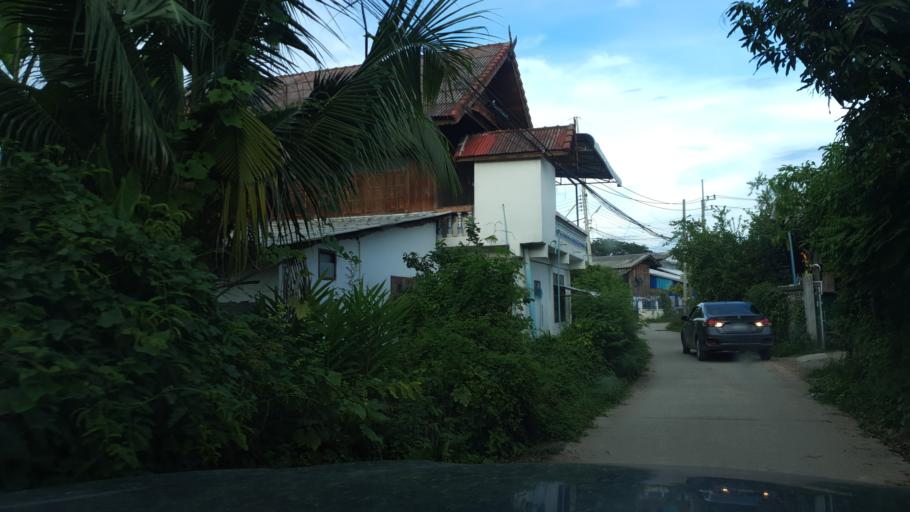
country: TH
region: Lamphun
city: Ban Thi
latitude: 18.6502
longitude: 99.1082
